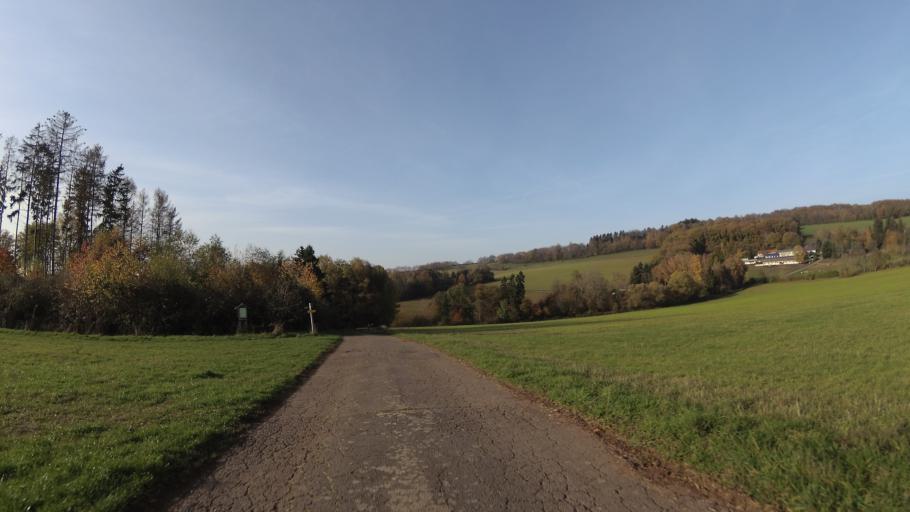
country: DE
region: Saarland
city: Hangard
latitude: 49.3903
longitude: 7.1930
